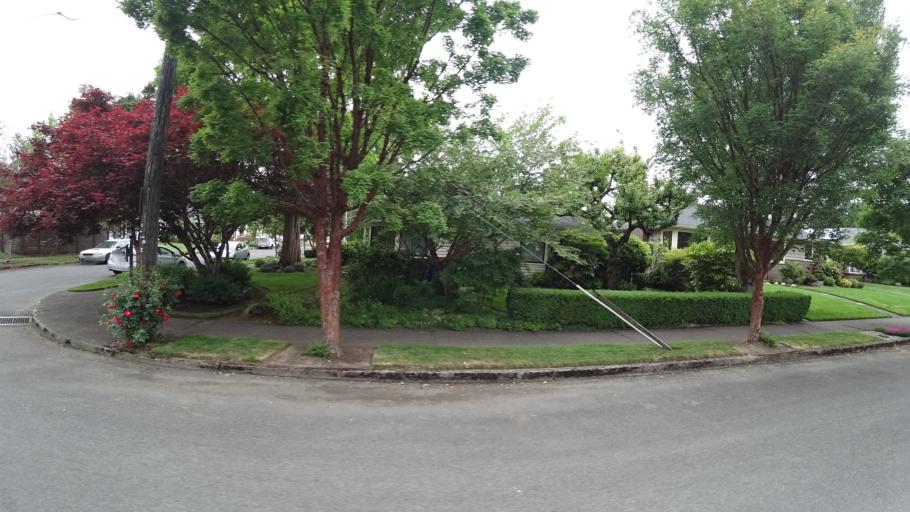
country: US
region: Oregon
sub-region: Multnomah County
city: Lents
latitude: 45.5202
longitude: -122.6139
